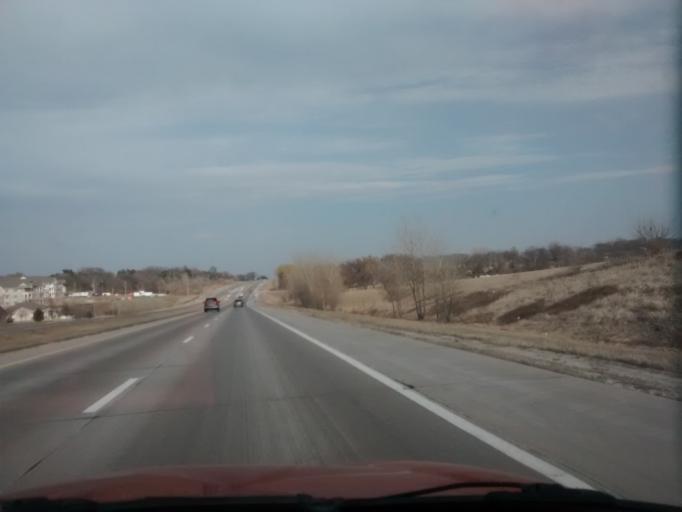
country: US
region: Nebraska
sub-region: Sarpy County
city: Papillion
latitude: 41.1379
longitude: -96.0102
